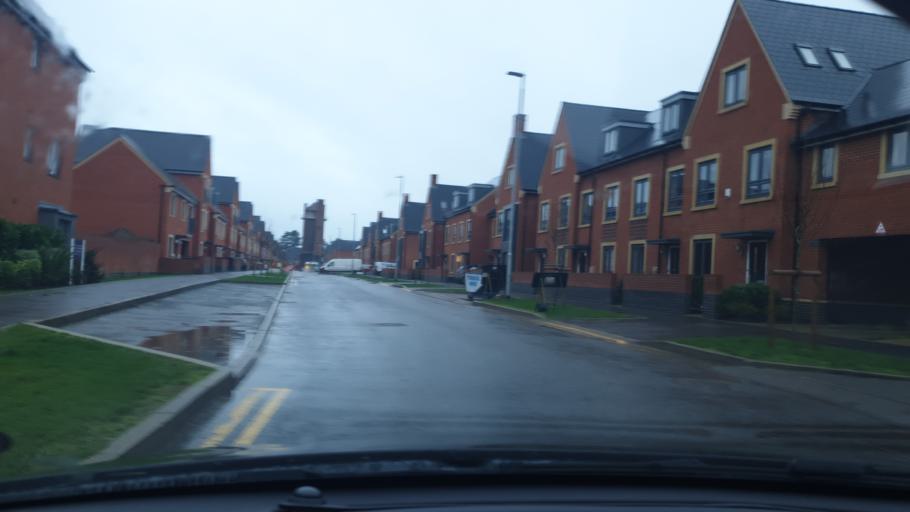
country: GB
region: England
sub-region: Essex
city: Colchester
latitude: 51.9188
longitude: 0.9004
